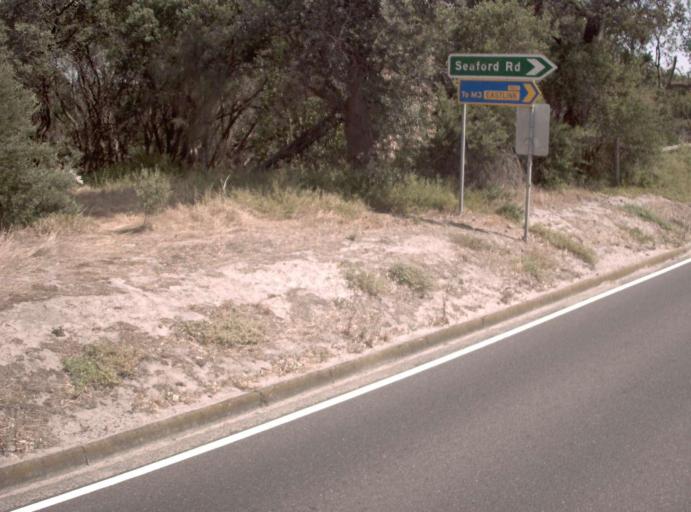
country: AU
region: Victoria
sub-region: Frankston
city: Seaford
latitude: -38.1107
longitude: 145.1257
